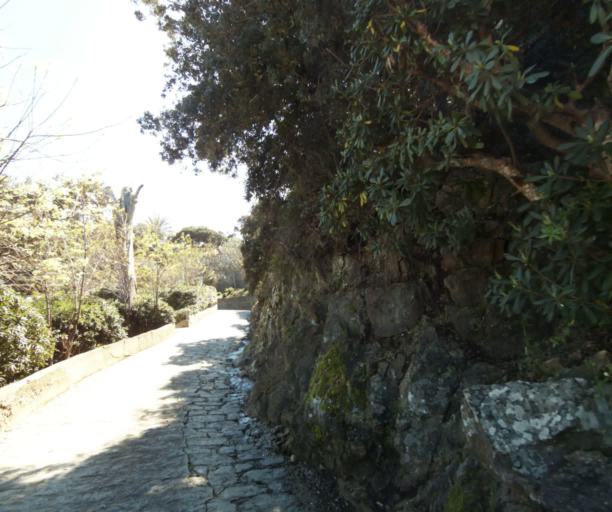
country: FR
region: Corsica
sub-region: Departement de la Corse-du-Sud
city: Propriano
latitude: 41.6794
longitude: 8.9141
